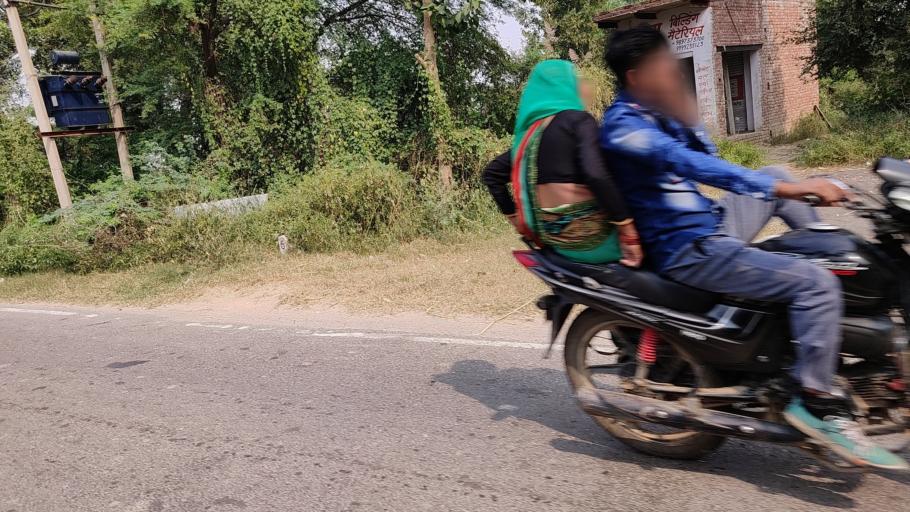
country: IN
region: Uttar Pradesh
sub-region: Mathura
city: Barsana
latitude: 27.6591
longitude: 77.3823
